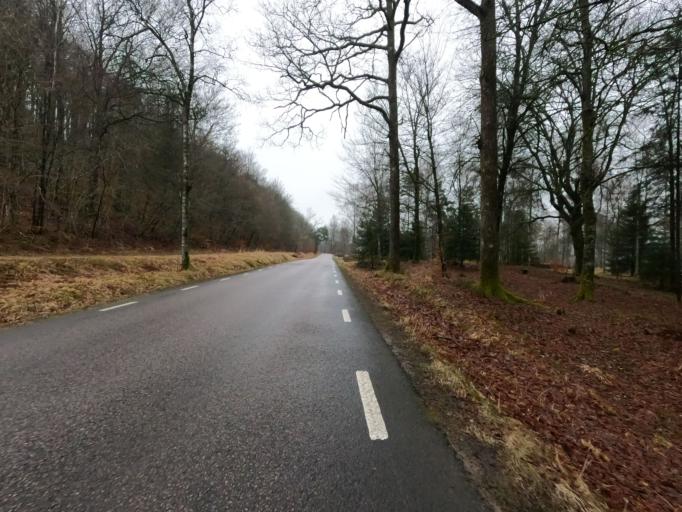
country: SE
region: Halland
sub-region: Halmstads Kommun
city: Oskarstrom
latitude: 56.7580
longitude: 13.1717
